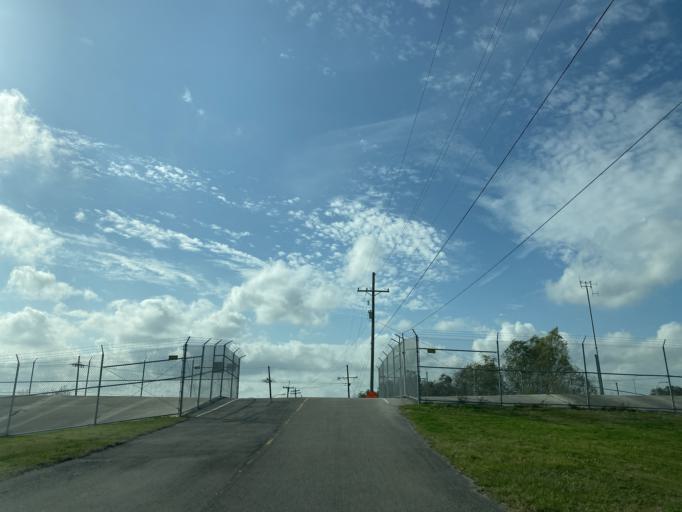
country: US
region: Louisiana
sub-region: Saint Bernard Parish
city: Arabi
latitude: 30.0305
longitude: -90.0365
